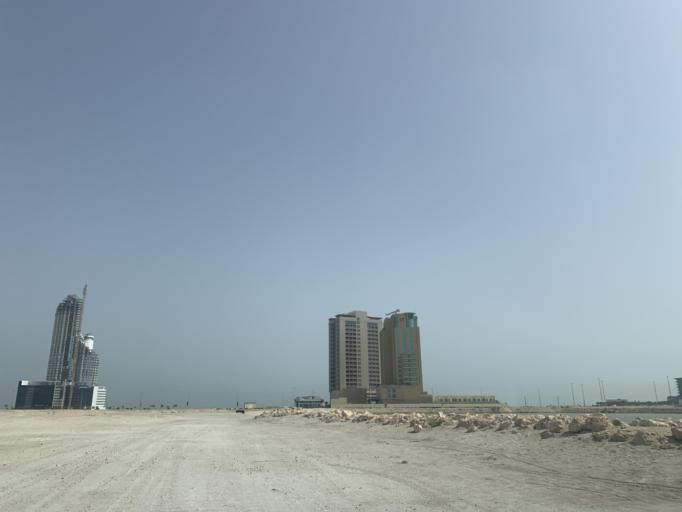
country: BH
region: Manama
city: Jidd Hafs
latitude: 26.2379
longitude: 50.5573
